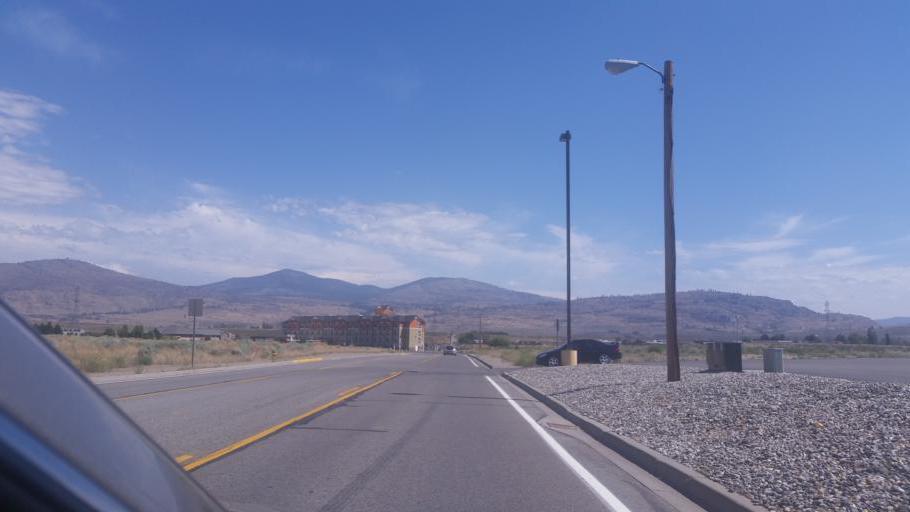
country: US
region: Washington
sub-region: Okanogan County
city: Omak
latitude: 48.4204
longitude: -119.5098
